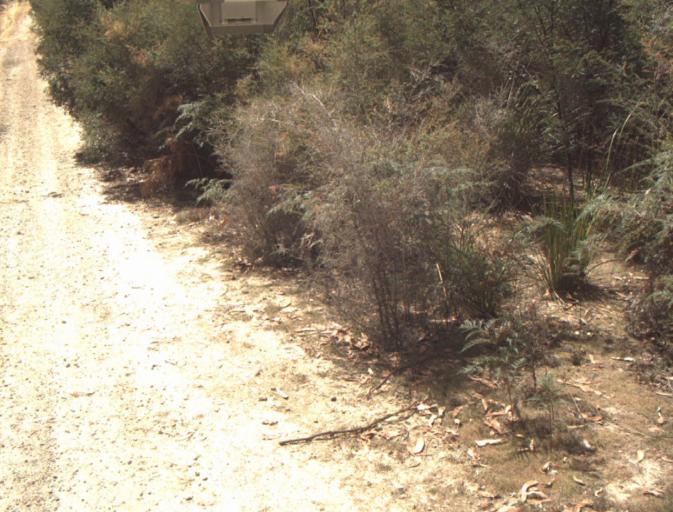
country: AU
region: Tasmania
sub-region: Launceston
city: Mayfield
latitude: -41.2044
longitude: 147.1599
